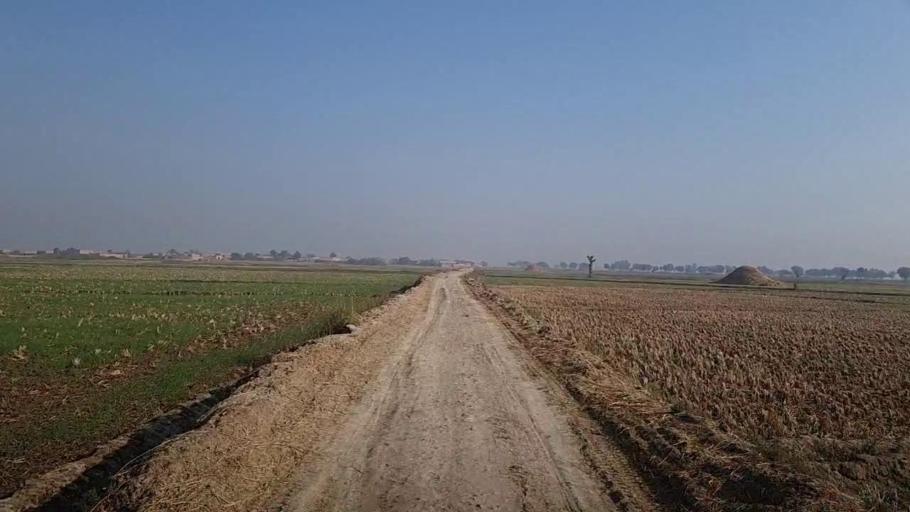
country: PK
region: Sindh
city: Radhan
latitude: 27.1133
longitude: 67.8934
